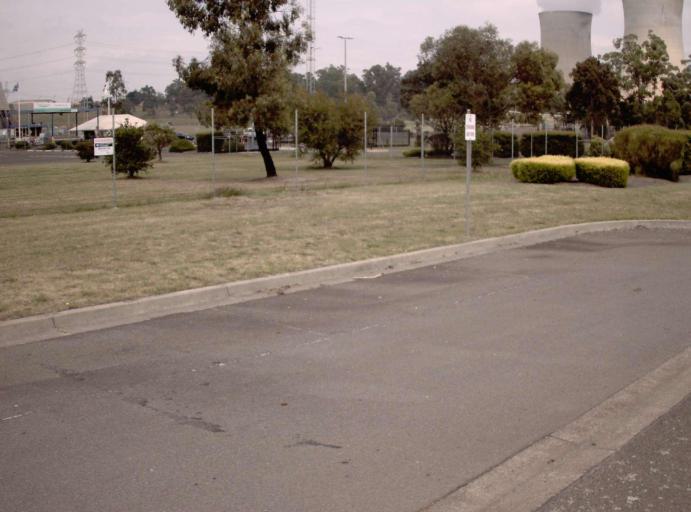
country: AU
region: Victoria
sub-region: Latrobe
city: Traralgon
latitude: -38.2529
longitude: 146.5858
